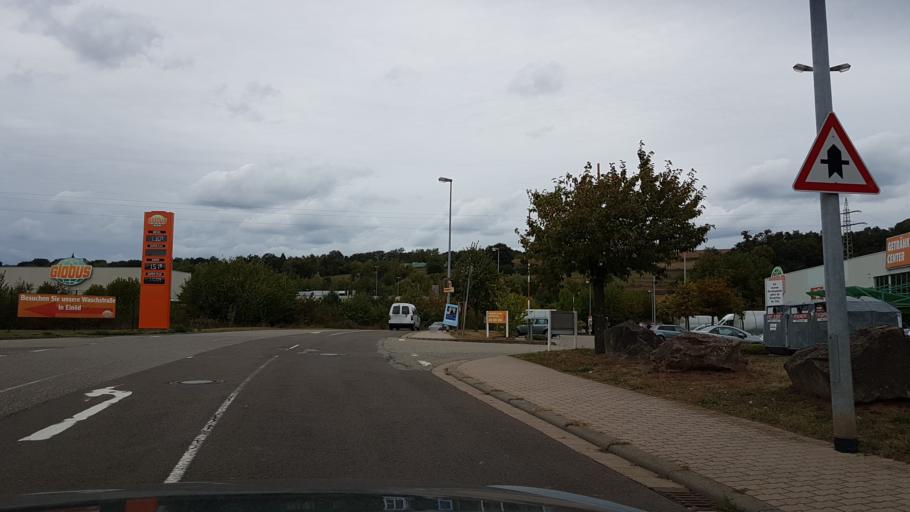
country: DE
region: Rheinland-Pfalz
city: Zweibrucken
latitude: 49.2615
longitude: 7.3374
